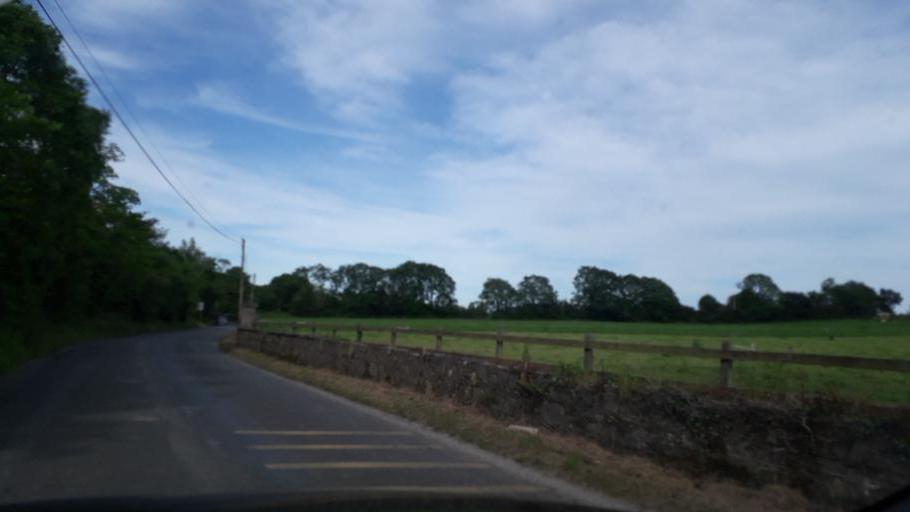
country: IE
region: Leinster
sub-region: Loch Garman
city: Ballinroad
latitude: 52.5180
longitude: -6.2795
